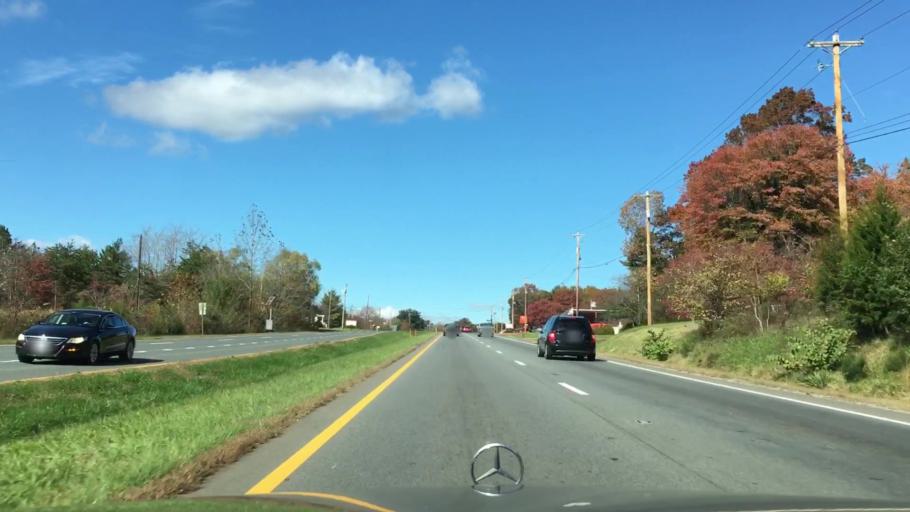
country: US
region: Virginia
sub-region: Campbell County
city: Timberlake
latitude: 37.3131
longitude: -79.1849
